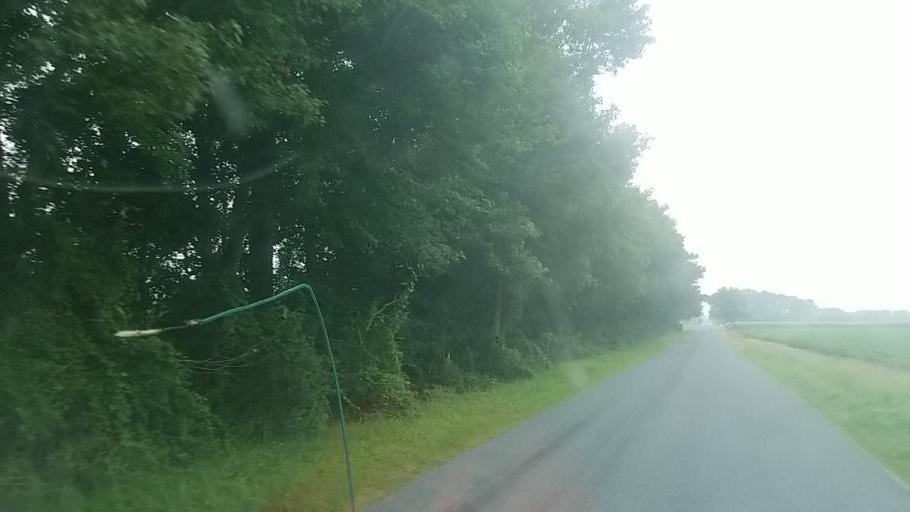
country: US
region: Maryland
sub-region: Wicomico County
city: Pittsville
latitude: 38.4521
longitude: -75.3741
